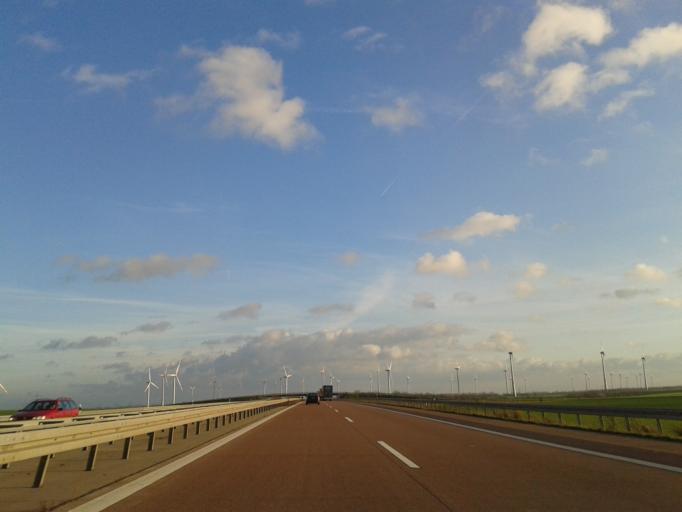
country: DE
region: Saxony-Anhalt
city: Obhausen
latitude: 51.4124
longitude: 11.6758
